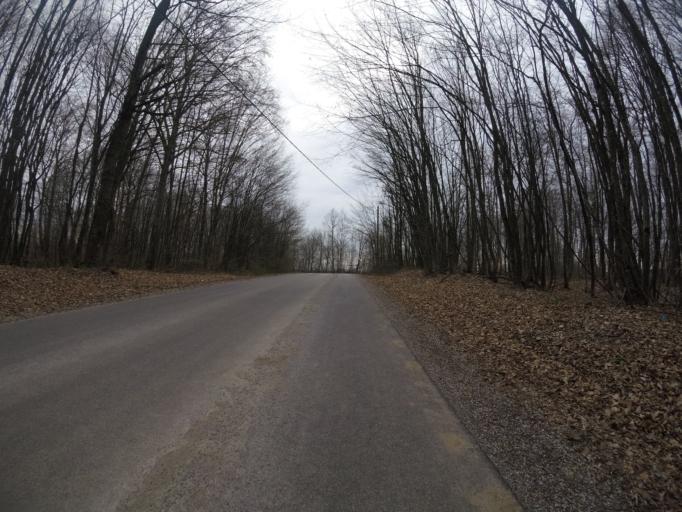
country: HR
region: Grad Zagreb
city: Strmec
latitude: 45.5980
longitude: 15.9111
